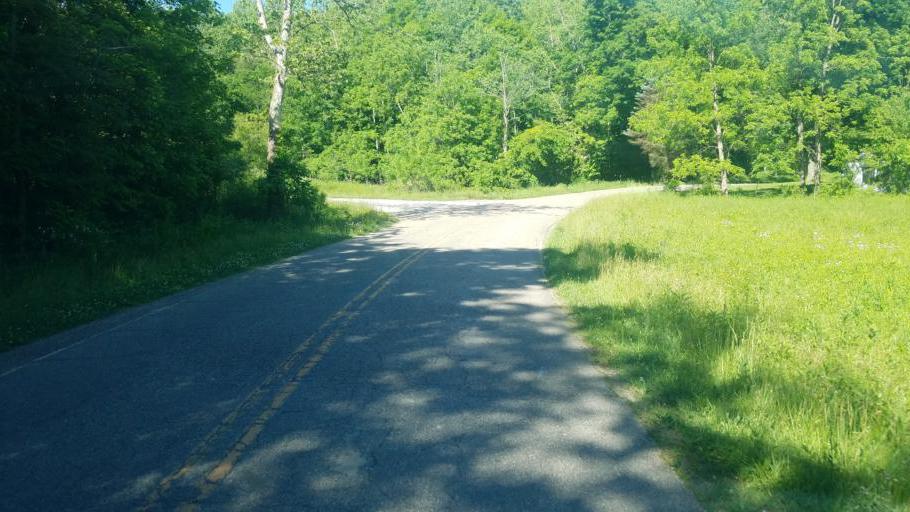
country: US
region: Ohio
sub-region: Tuscarawas County
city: Newcomerstown
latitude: 40.1836
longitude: -81.6093
